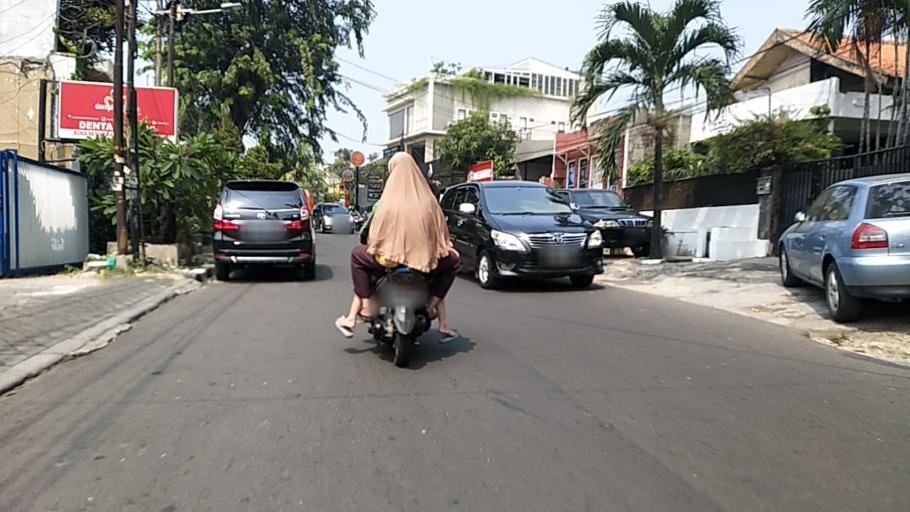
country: ID
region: Jakarta Raya
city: Jakarta
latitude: -6.2347
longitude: 106.8485
